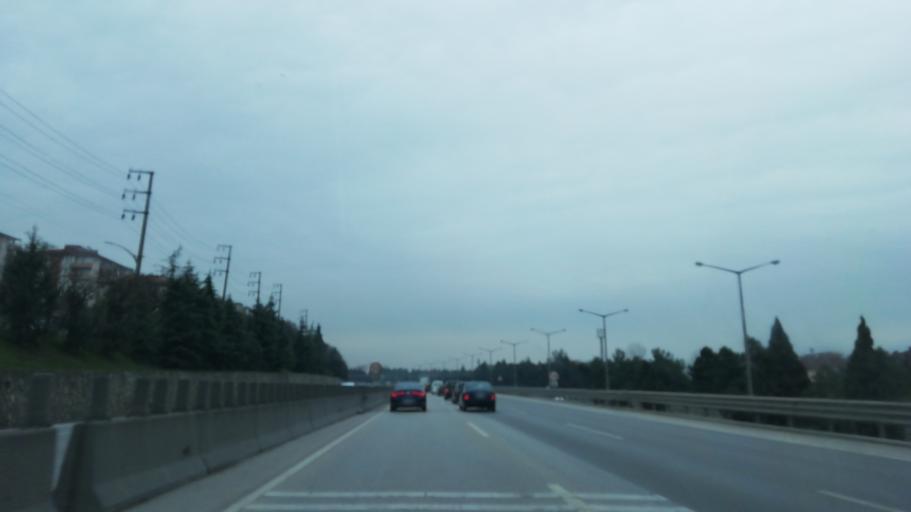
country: TR
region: Kocaeli
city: Izmit
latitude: 40.7616
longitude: 29.8672
